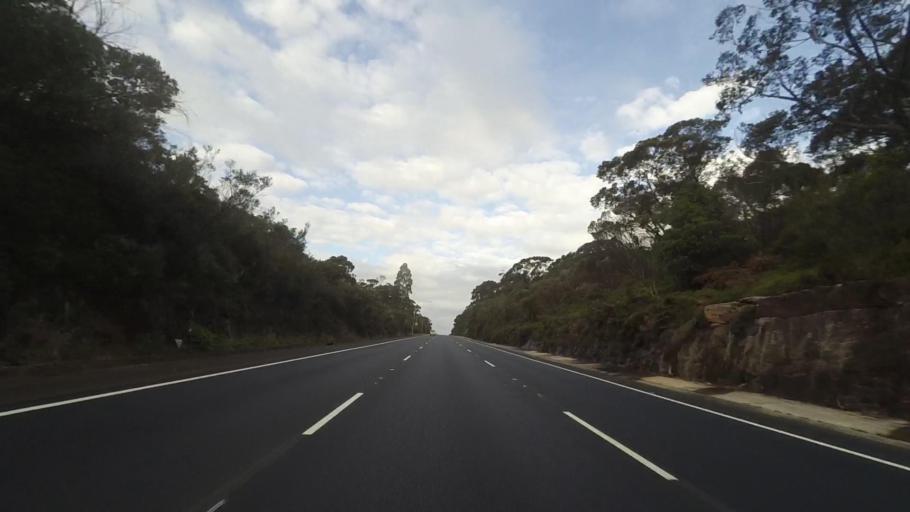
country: AU
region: New South Wales
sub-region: Wollongong
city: Bulli
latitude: -34.3021
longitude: 150.9070
